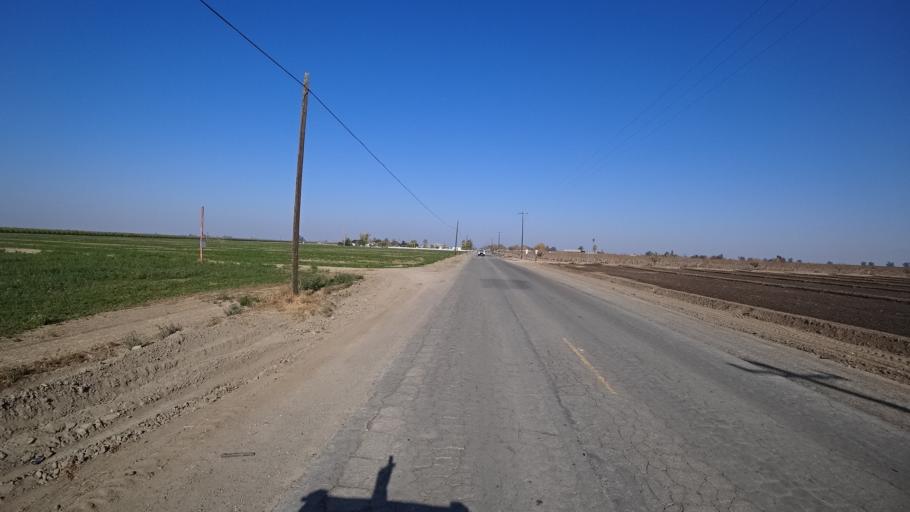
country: US
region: California
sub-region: Kern County
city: Greenfield
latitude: 35.2482
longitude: -119.0391
